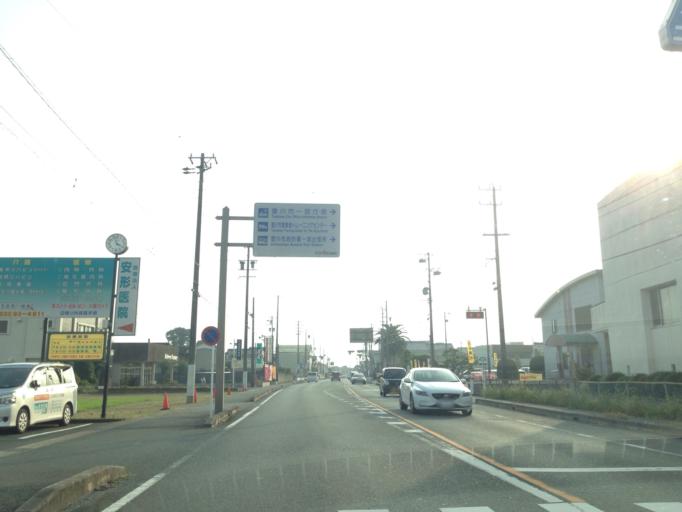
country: JP
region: Aichi
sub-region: Tokai-shi
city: Toyokawa
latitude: 34.8565
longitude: 137.4244
